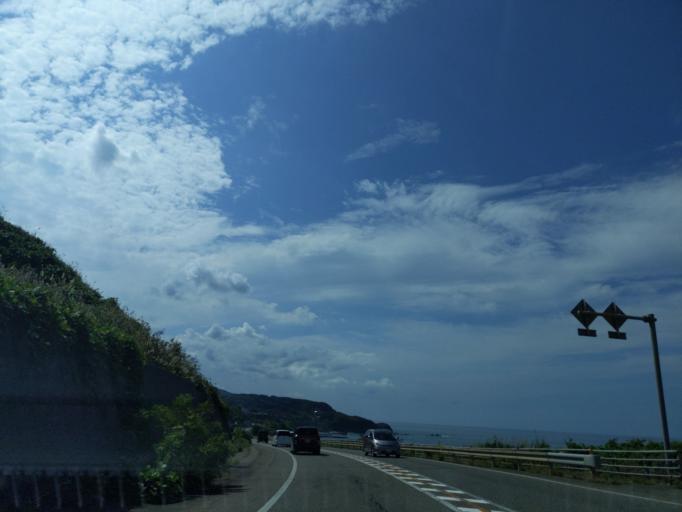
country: JP
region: Niigata
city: Kashiwazaki
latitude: 37.3436
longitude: 138.4807
